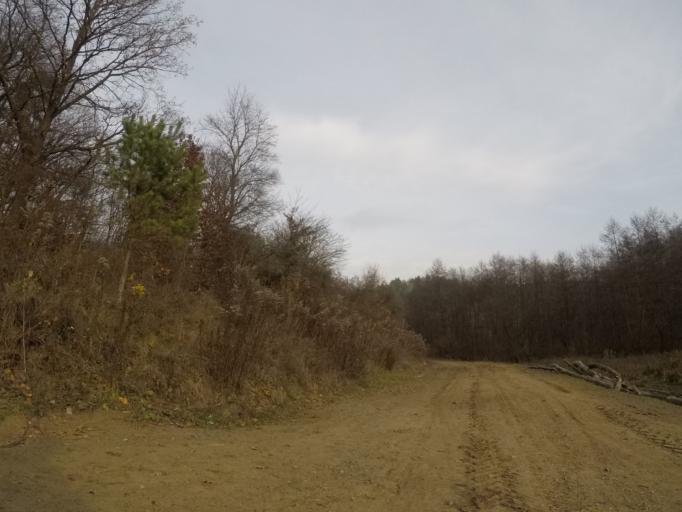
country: SK
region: Presovsky
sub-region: Okres Presov
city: Presov
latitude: 48.9480
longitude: 21.1960
